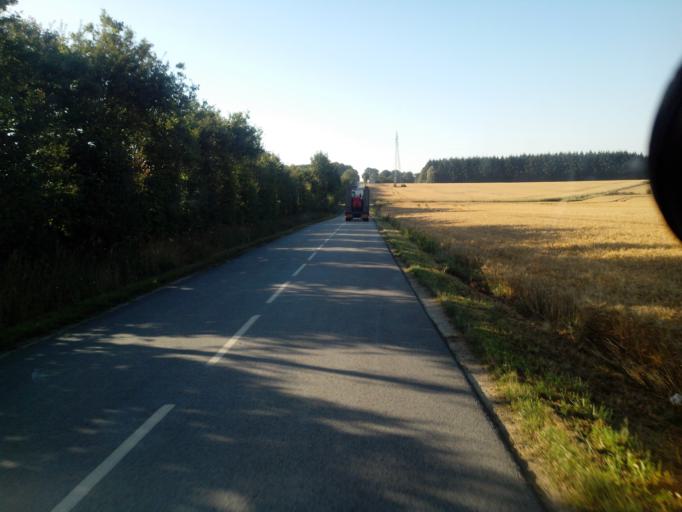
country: FR
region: Brittany
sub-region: Departement du Morbihan
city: Meneac
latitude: 48.0859
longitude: -2.4476
